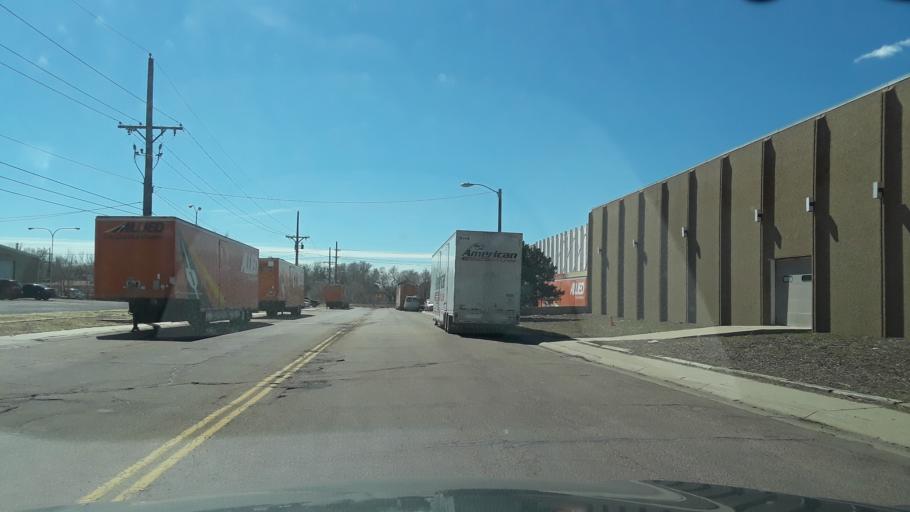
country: US
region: Colorado
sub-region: El Paso County
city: Colorado Springs
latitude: 38.8717
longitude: -104.8132
